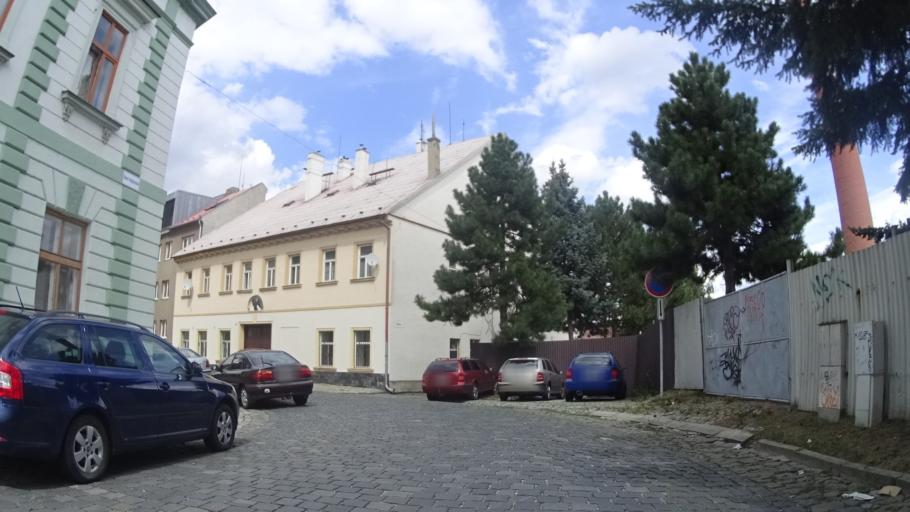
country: CZ
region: Olomoucky
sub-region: Okres Olomouc
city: Olomouc
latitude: 49.6033
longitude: 17.2426
